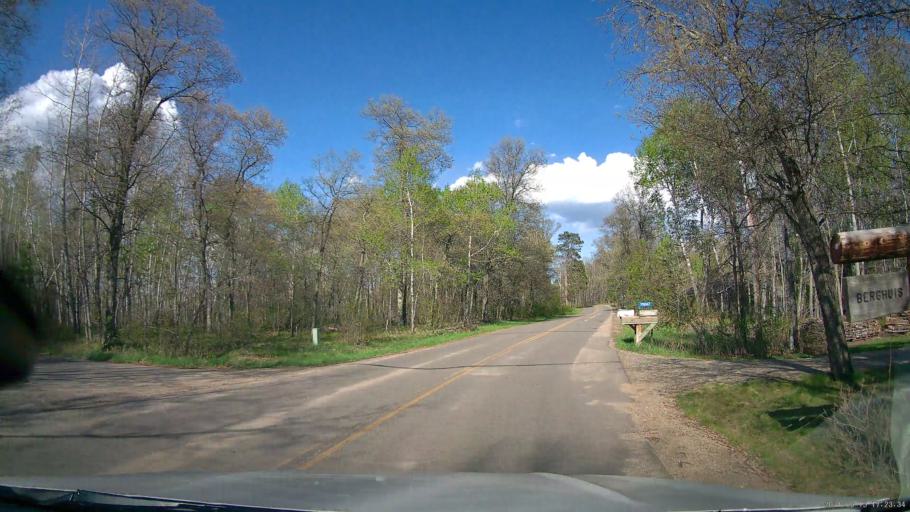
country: US
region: Minnesota
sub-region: Hubbard County
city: Park Rapids
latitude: 46.9909
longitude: -94.9666
